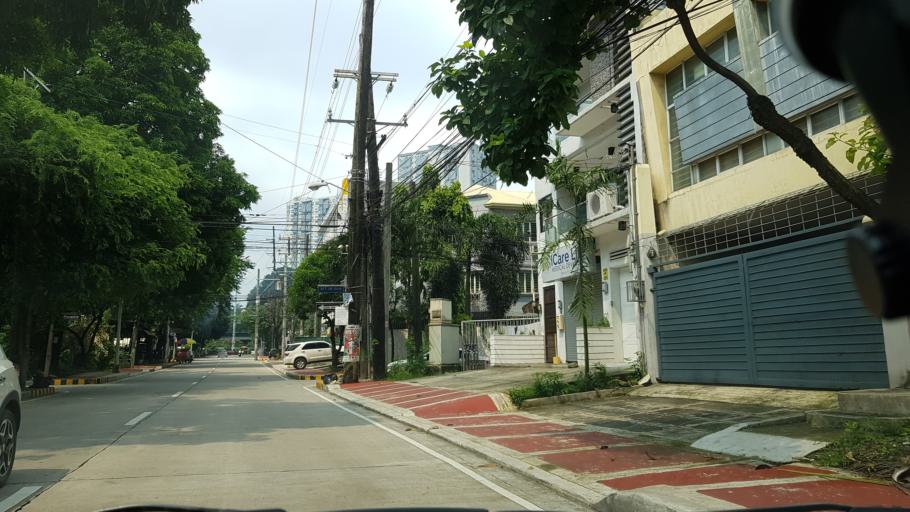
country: PH
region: Calabarzon
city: Del Monte
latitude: 14.6327
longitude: 121.0260
